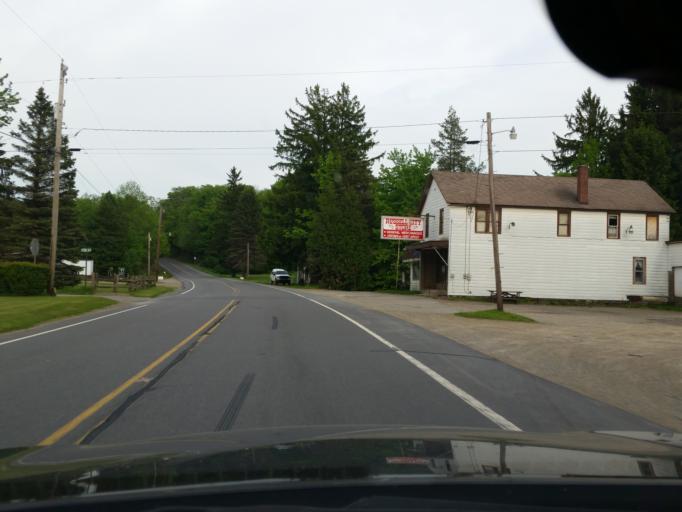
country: US
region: Pennsylvania
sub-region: McKean County
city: Kane
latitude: 41.5714
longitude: -78.9091
